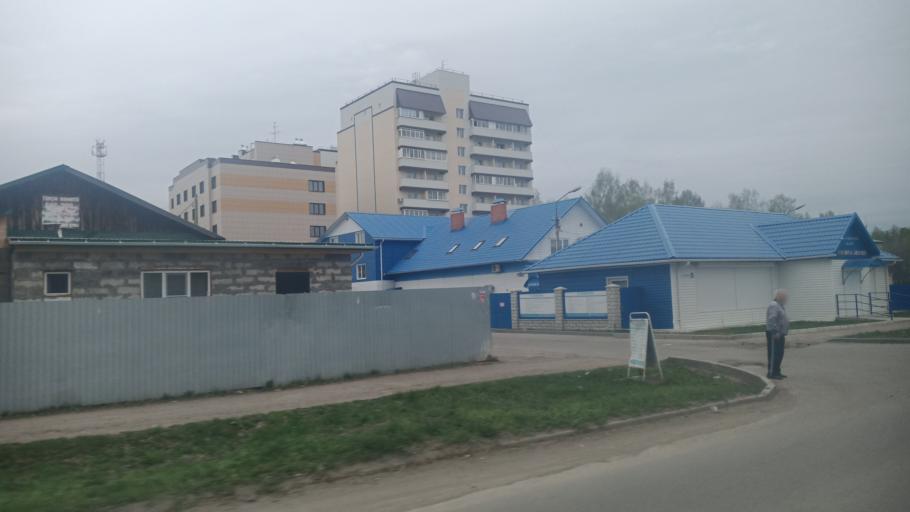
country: RU
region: Altai Krai
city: Yuzhnyy
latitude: 53.2533
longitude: 83.6855
